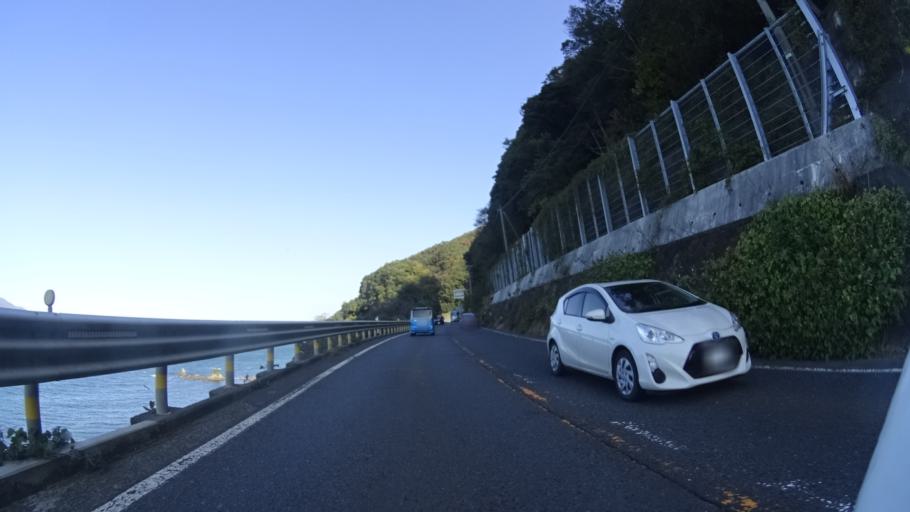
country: JP
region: Fukui
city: Tsuruga
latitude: 35.6909
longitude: 136.0815
